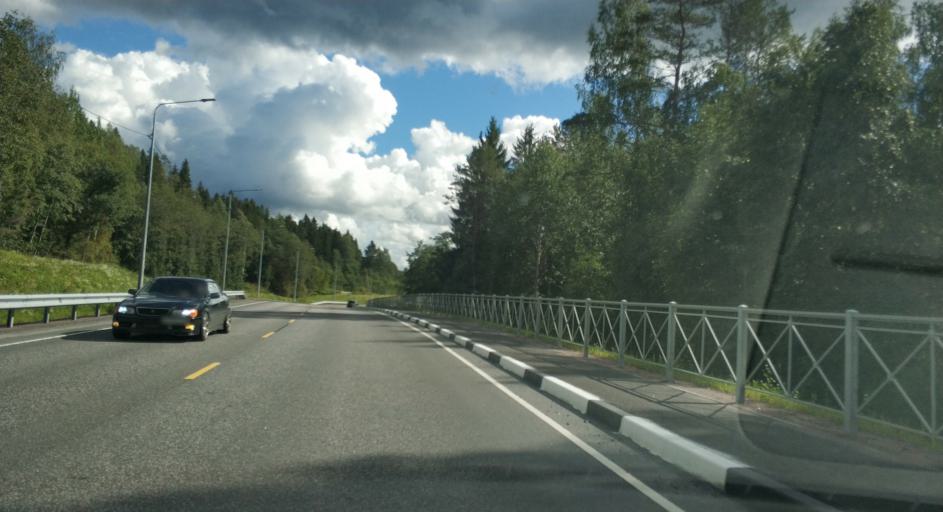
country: RU
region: Republic of Karelia
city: Ruskeala
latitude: 61.9240
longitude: 30.6024
